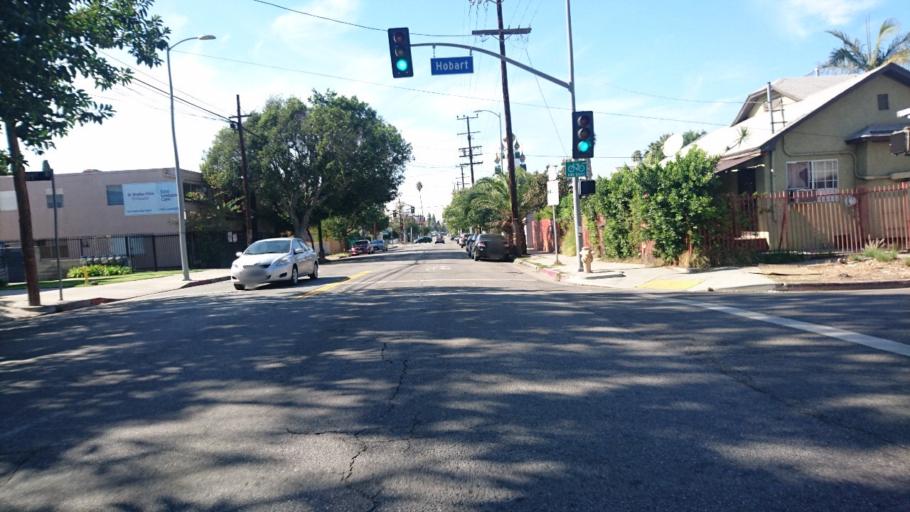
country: US
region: California
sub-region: Los Angeles County
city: Hollywood
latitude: 34.0951
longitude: -118.3056
